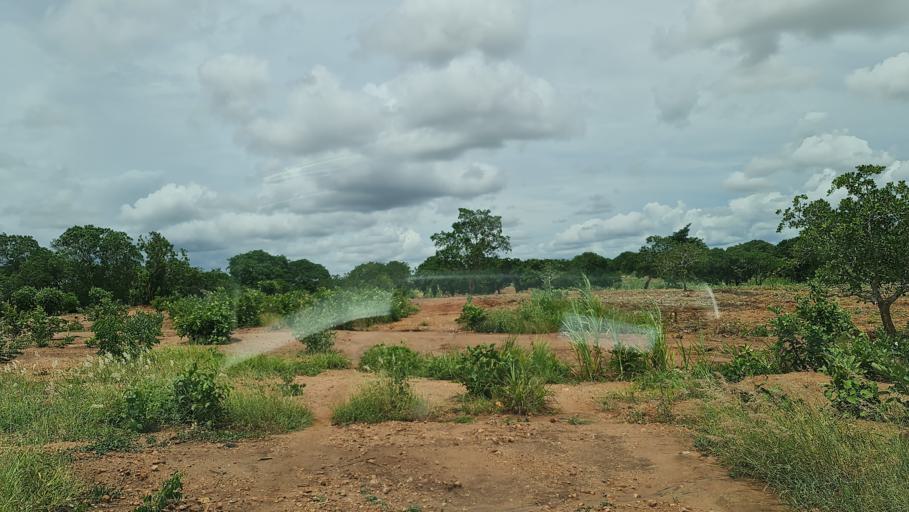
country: MZ
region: Nampula
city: Nacala
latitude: -14.7783
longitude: 39.9925
